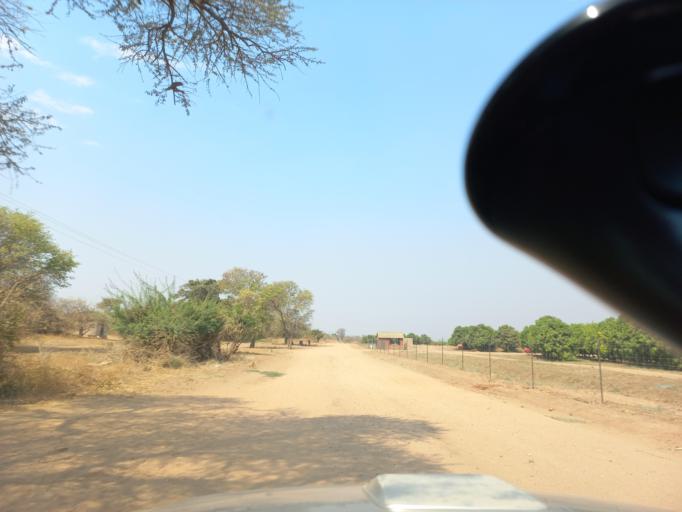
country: ZW
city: Chirundu
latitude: -15.9324
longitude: 28.9492
